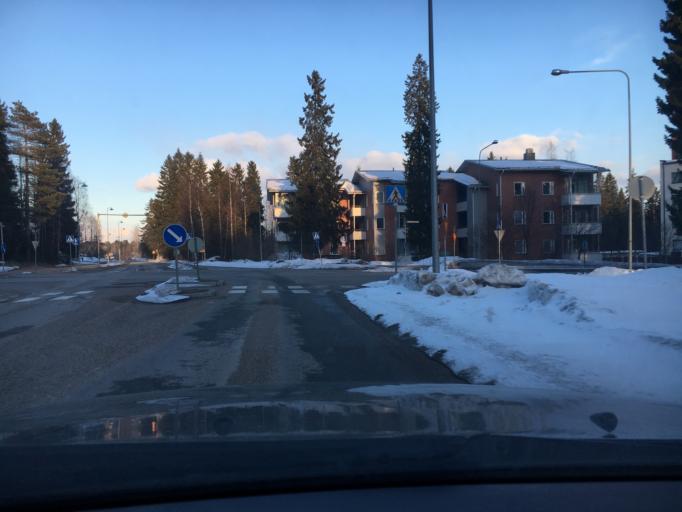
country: FI
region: Kainuu
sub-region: Kajaani
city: Kajaani
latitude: 64.2299
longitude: 27.7523
